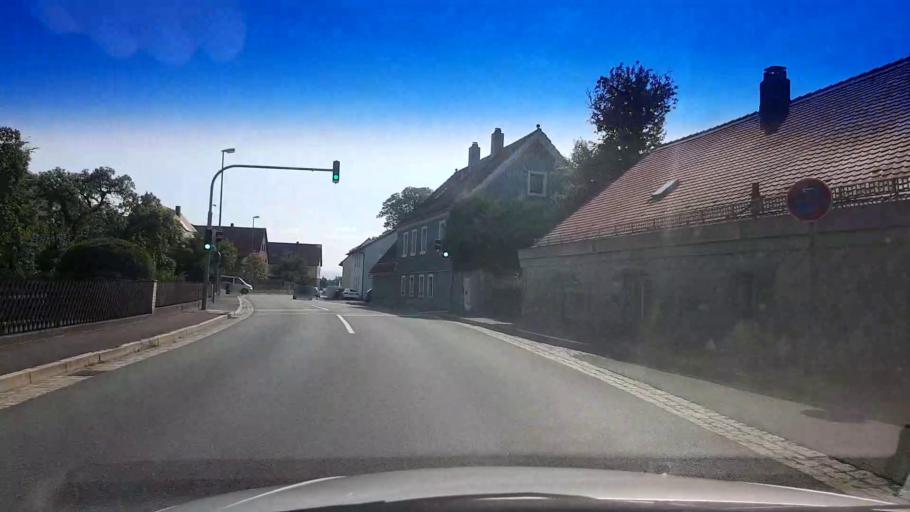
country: DE
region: Bavaria
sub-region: Upper Franconia
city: Eckersdorf
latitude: 49.9341
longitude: 11.5129
